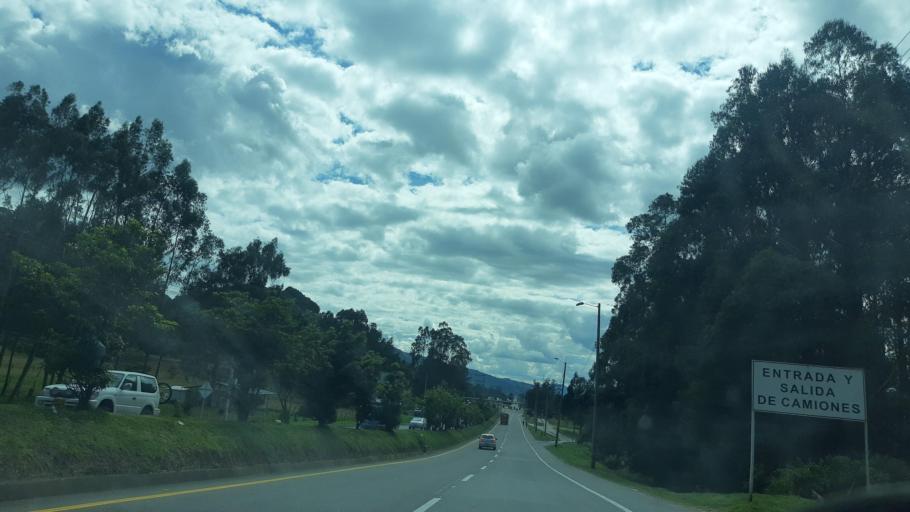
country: CO
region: Cundinamarca
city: Sesquile
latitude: 5.0364
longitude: -73.8358
